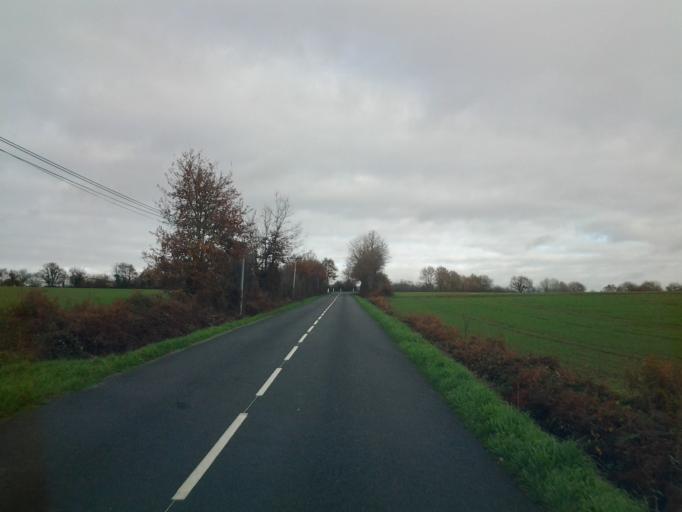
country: FR
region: Pays de la Loire
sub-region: Departement de la Vendee
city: Bournezeau
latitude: 46.6251
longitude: -1.1945
